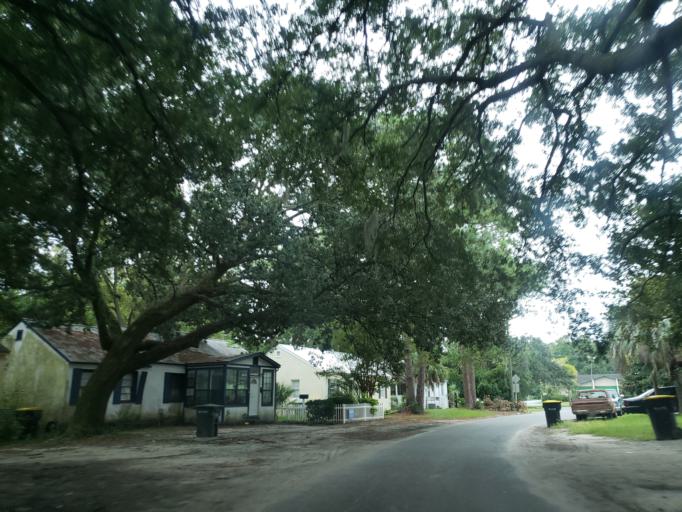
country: US
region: Georgia
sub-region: Chatham County
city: Thunderbolt
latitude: 32.0457
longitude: -81.0730
